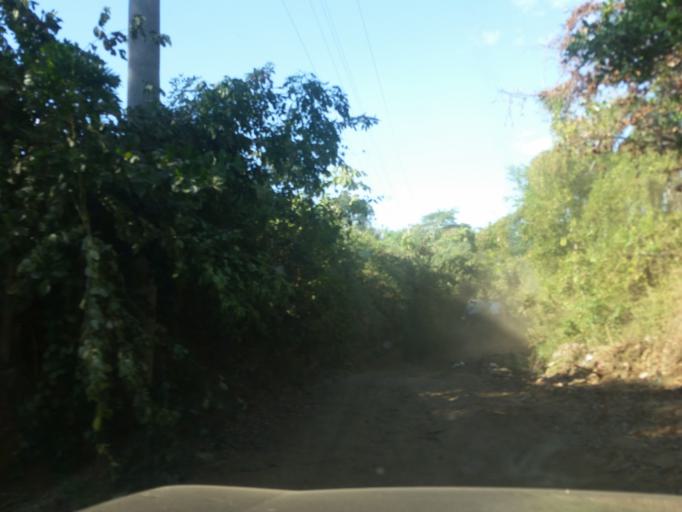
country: NI
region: Managua
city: Managua
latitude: 12.0719
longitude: -86.2537
